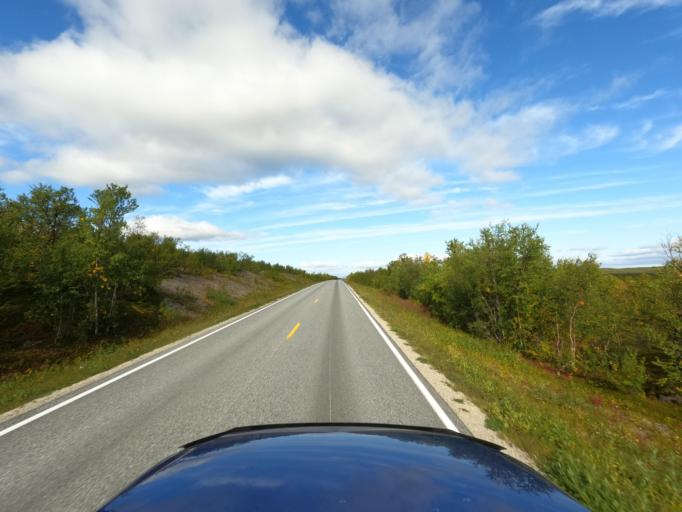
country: NO
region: Finnmark Fylke
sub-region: Karasjok
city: Karasjohka
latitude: 69.6523
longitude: 25.2791
